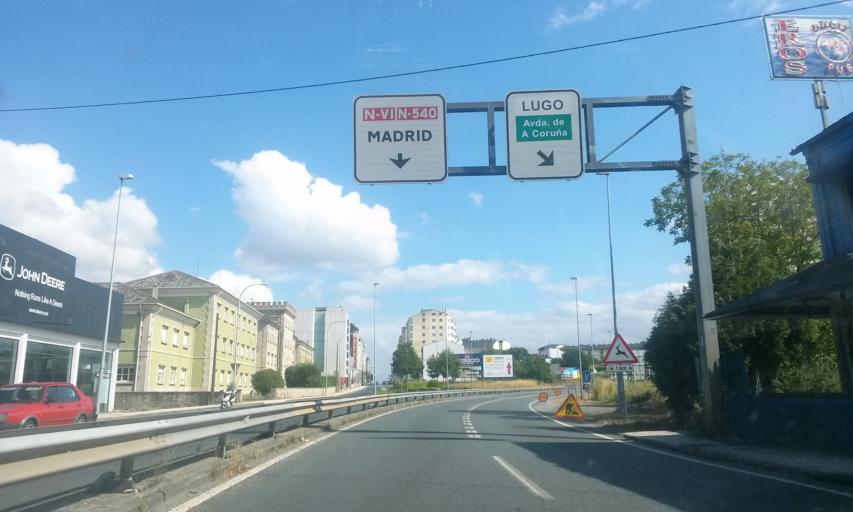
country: ES
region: Galicia
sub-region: Provincia de Lugo
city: Lugo
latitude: 43.0335
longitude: -7.5736
